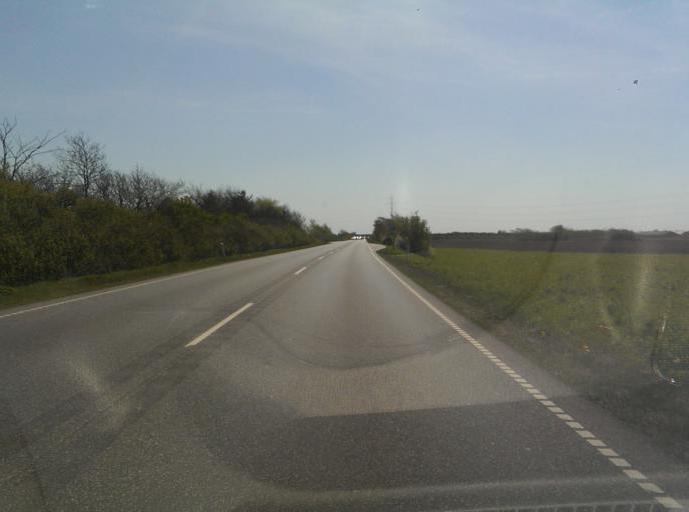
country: DK
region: South Denmark
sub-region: Esbjerg Kommune
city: Bramming
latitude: 55.4157
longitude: 8.7139
